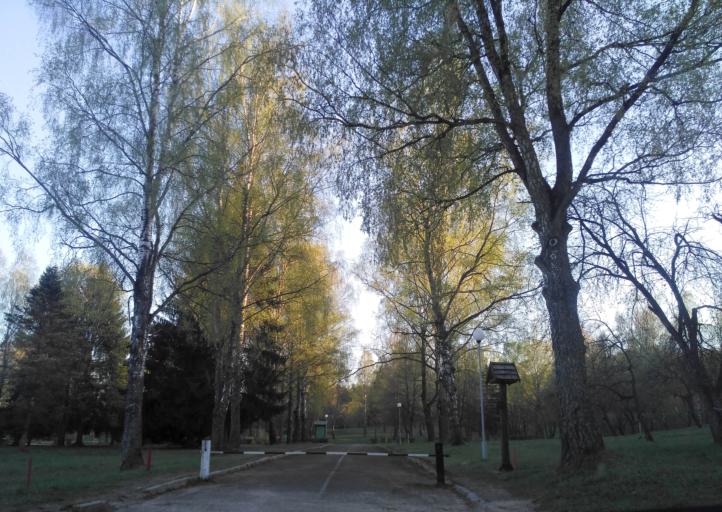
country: BY
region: Minsk
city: Pyatryshki
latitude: 54.0925
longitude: 27.1938
